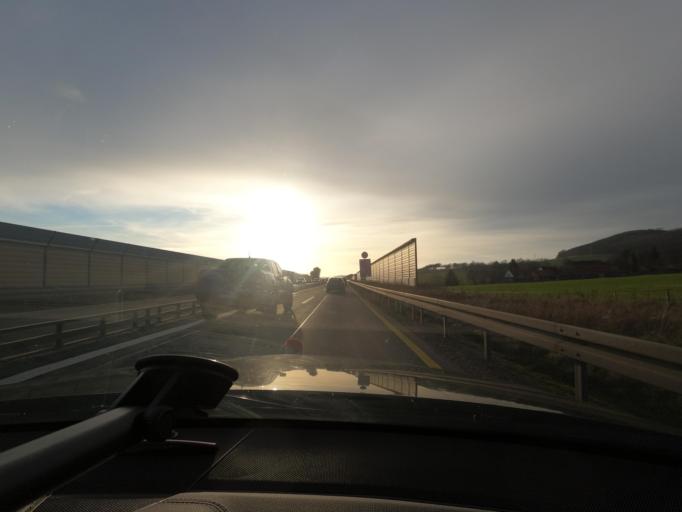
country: DE
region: Lower Saxony
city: Kalefeld
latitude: 51.8120
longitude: 10.1003
